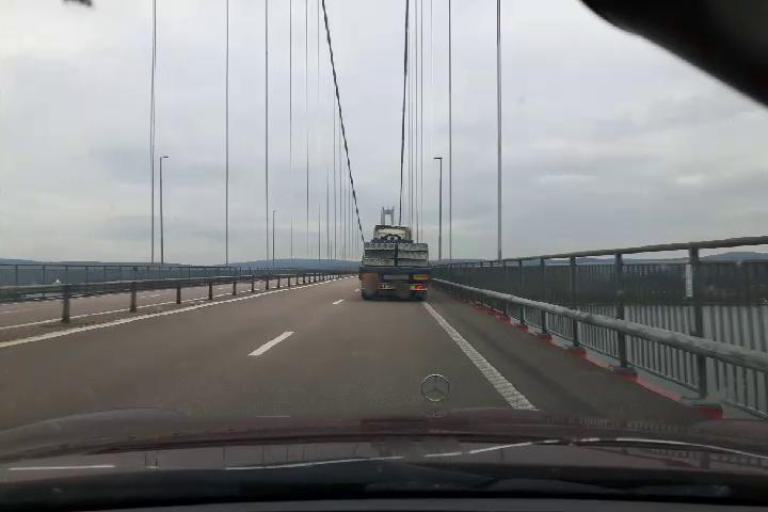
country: SE
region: Vaesternorrland
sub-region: Haernoesands Kommun
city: Haernoesand
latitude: 62.8001
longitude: 17.9416
